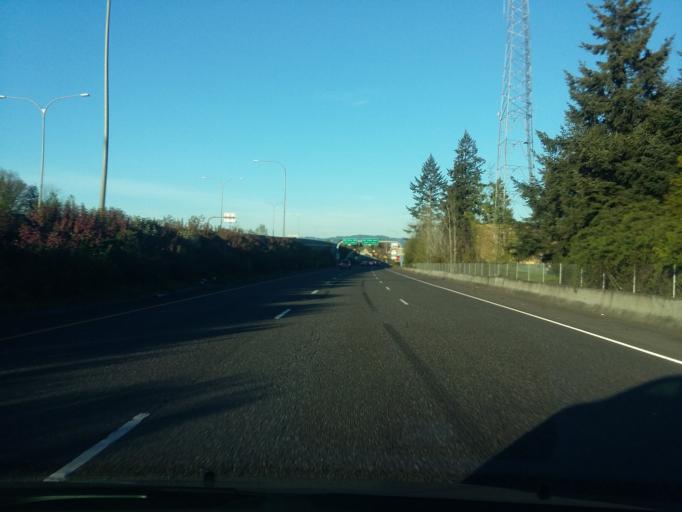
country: US
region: Washington
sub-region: Clark County
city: Orchards
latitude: 45.6599
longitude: -122.5625
